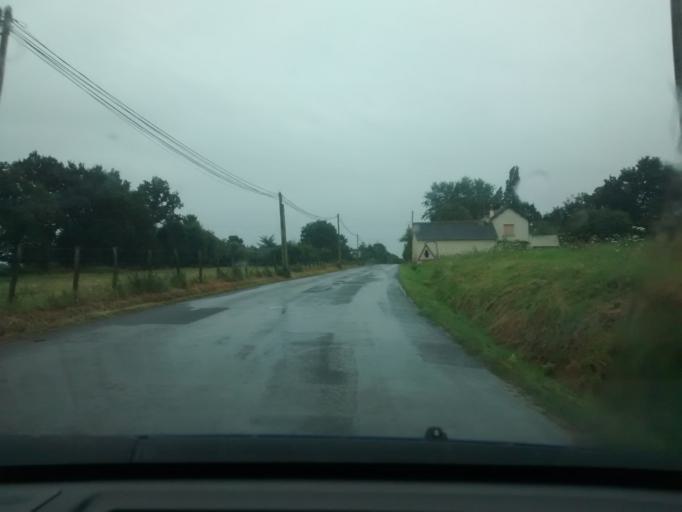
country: FR
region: Brittany
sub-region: Departement d'Ille-et-Vilaine
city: Betton
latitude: 48.1701
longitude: -1.6221
